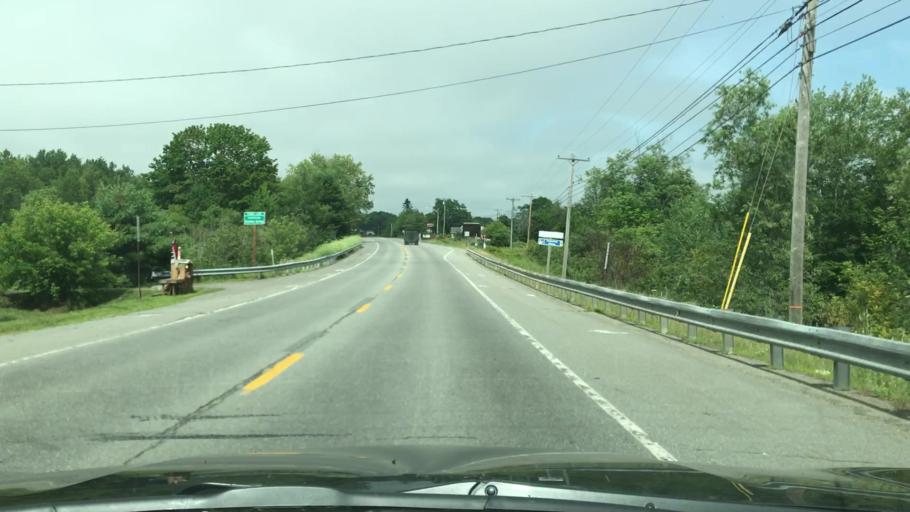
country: US
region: Maine
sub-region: Waldo County
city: Stockton Springs
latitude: 44.4843
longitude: -68.8665
